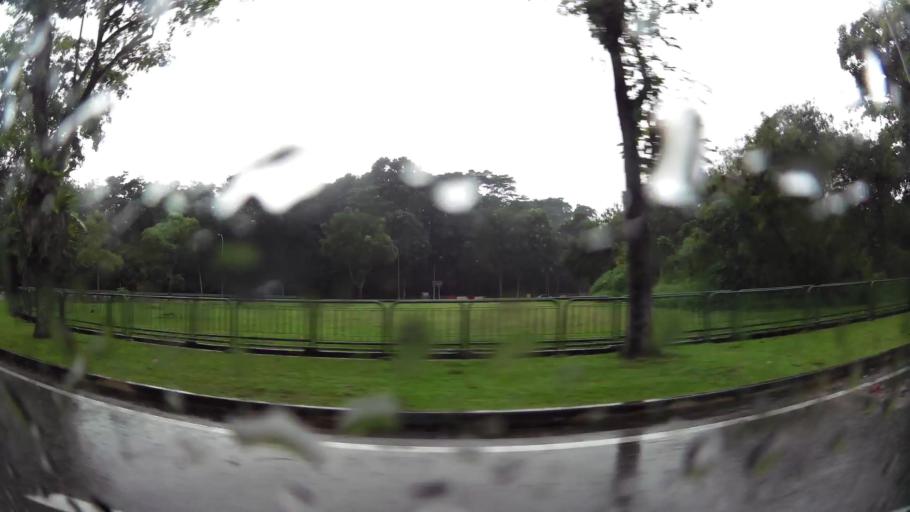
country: MY
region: Johor
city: Kampung Pasir Gudang Baru
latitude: 1.3720
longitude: 103.9390
